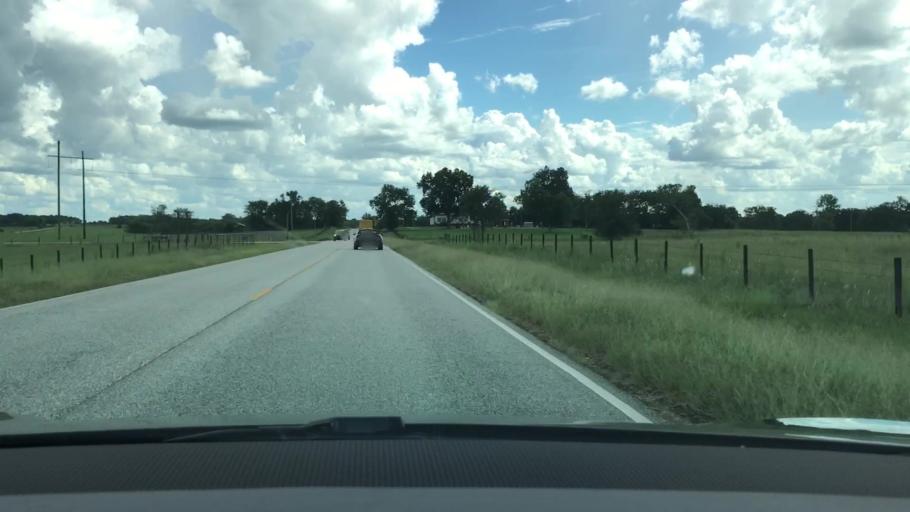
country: US
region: Alabama
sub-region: Montgomery County
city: Pike Road
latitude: 32.2632
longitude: -86.0990
